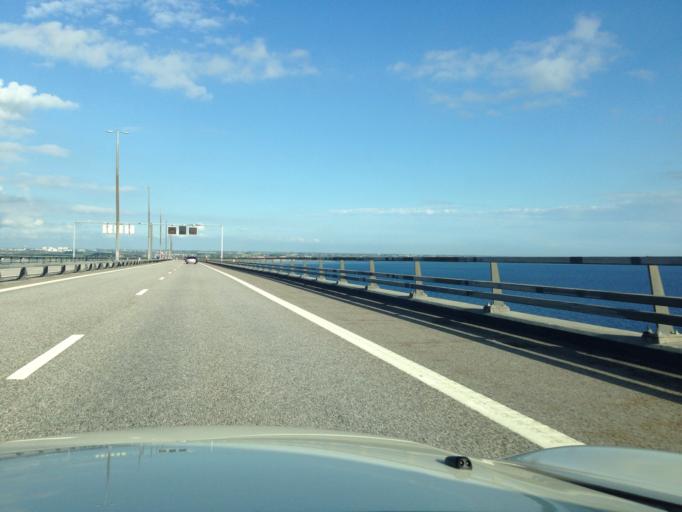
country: SE
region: Skane
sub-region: Malmo
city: Bunkeflostrand
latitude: 55.5701
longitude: 12.8510
